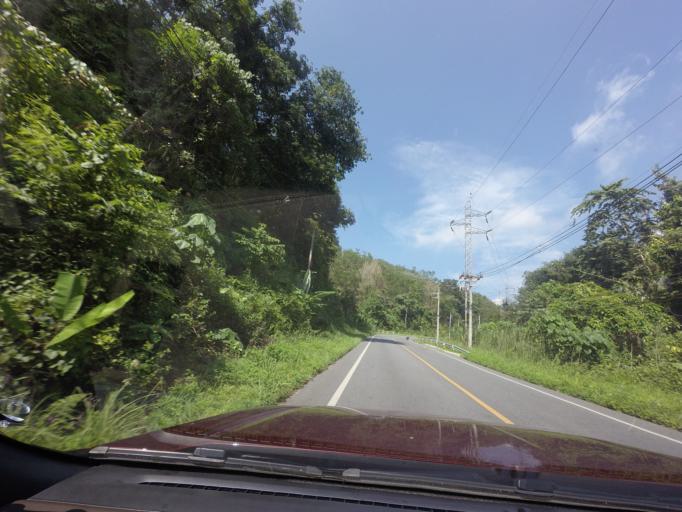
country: TH
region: Yala
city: Betong
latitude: 5.8821
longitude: 101.1404
